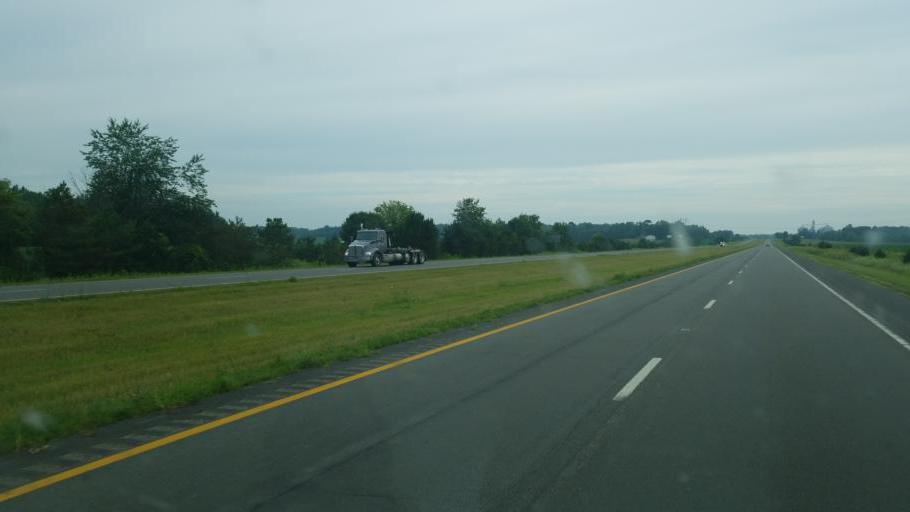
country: US
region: Ohio
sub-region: Knox County
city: Fredericktown
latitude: 40.4972
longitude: -82.5565
